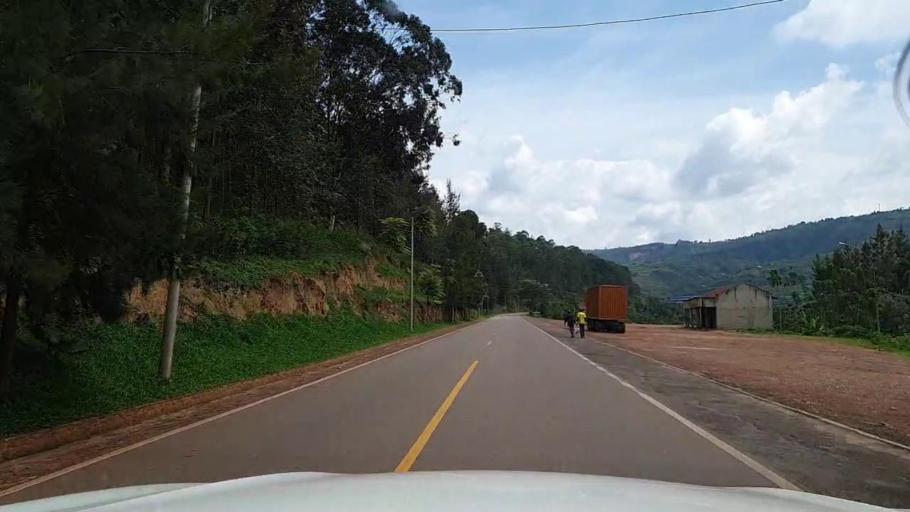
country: RW
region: Kigali
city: Kigali
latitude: -1.8618
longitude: 30.0890
